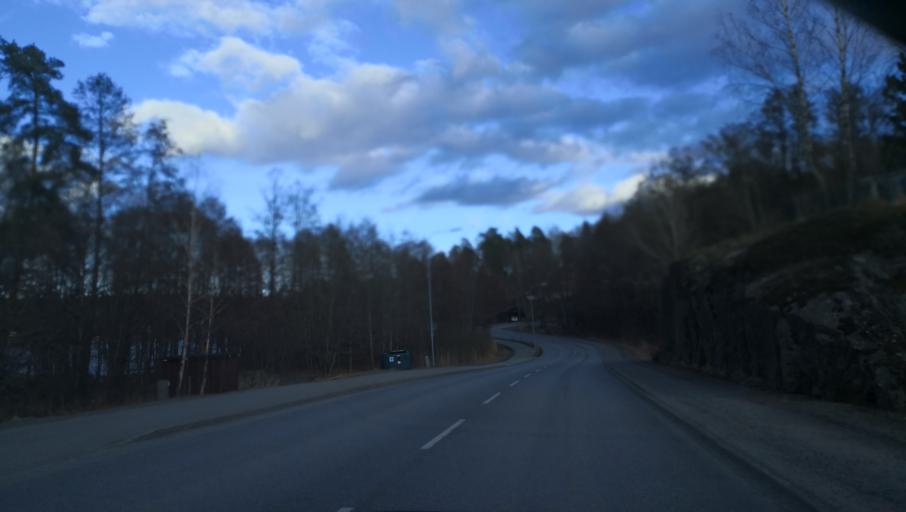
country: SE
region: Stockholm
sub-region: Nacka Kommun
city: Boo
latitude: 59.3335
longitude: 18.3287
